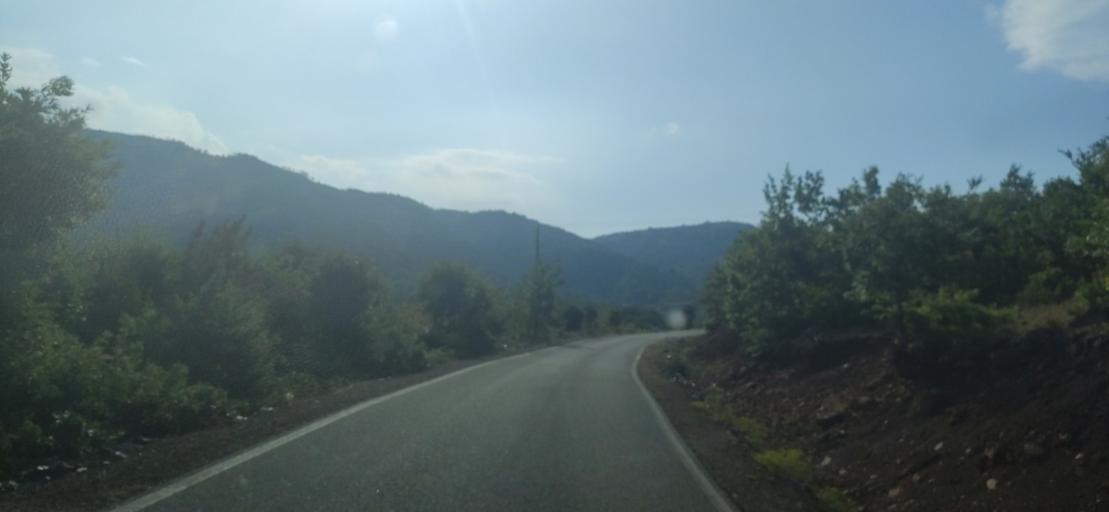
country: AL
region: Shkoder
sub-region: Rrethi i Pukes
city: Iballe
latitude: 42.1818
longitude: 19.9983
